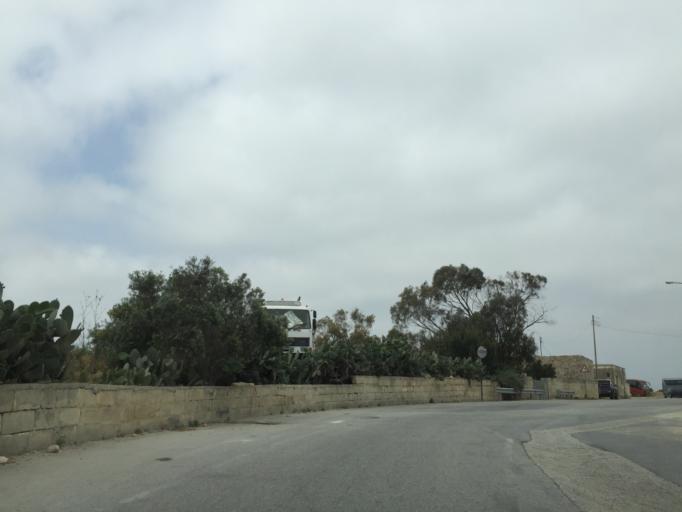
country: MT
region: Ir-Rabat
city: Rabat
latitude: 35.8861
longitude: 14.3925
